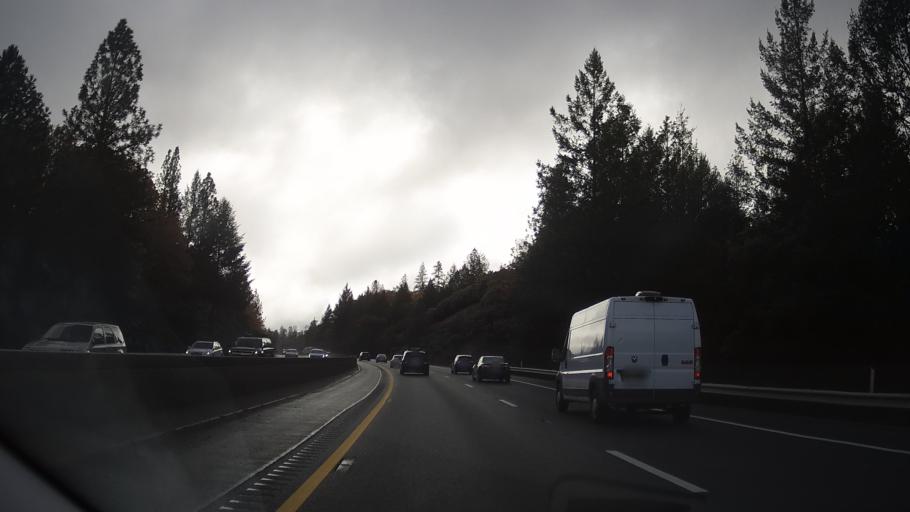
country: US
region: California
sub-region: Placer County
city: Colfax
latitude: 39.0634
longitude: -120.9671
